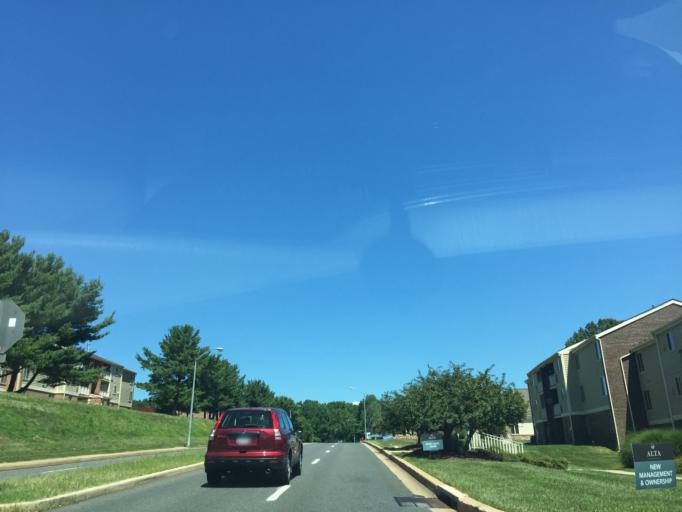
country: US
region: Maryland
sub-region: Baltimore County
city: Carney
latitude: 39.3831
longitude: -76.5102
